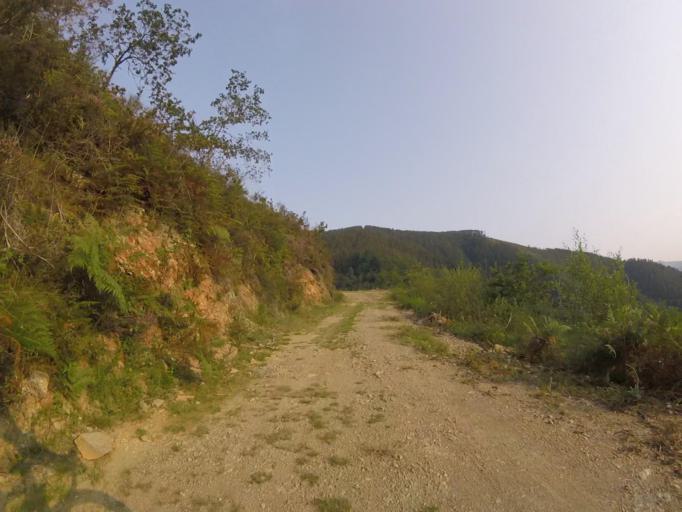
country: ES
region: Navarre
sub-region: Provincia de Navarra
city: Arano
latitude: 43.2491
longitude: -1.8657
